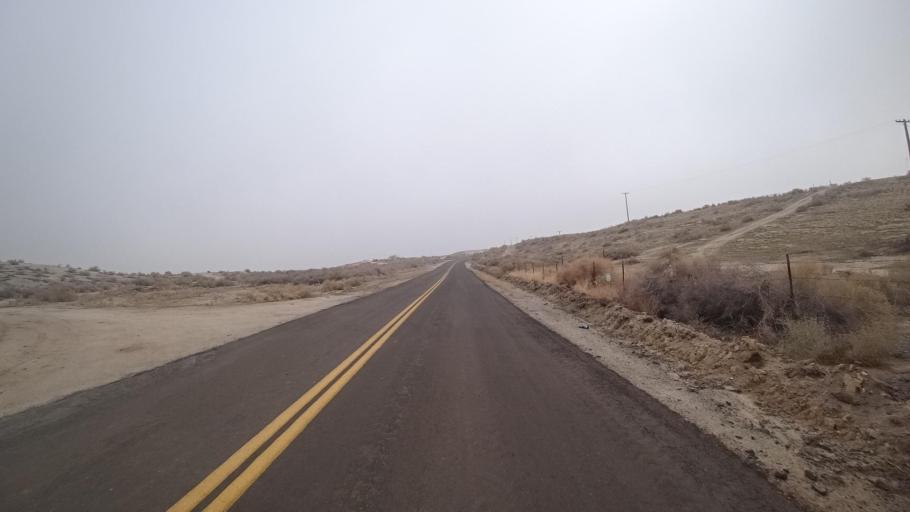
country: US
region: California
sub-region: Kern County
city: Ford City
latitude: 35.1634
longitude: -119.3796
